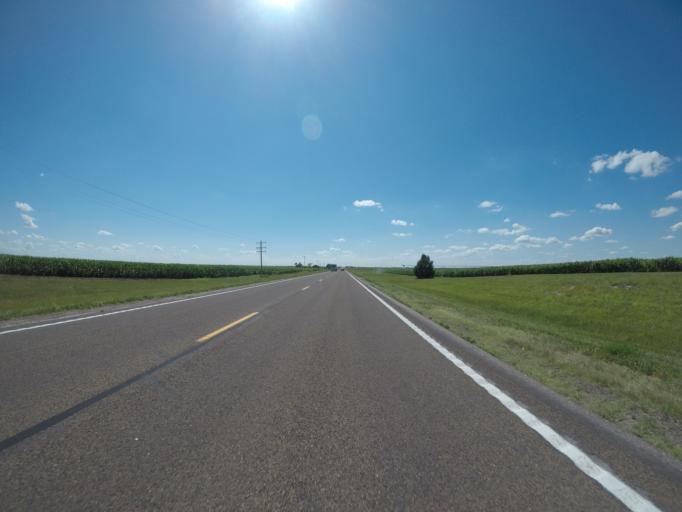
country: US
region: Nebraska
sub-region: Chase County
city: Imperial
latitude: 40.5375
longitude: -101.8115
